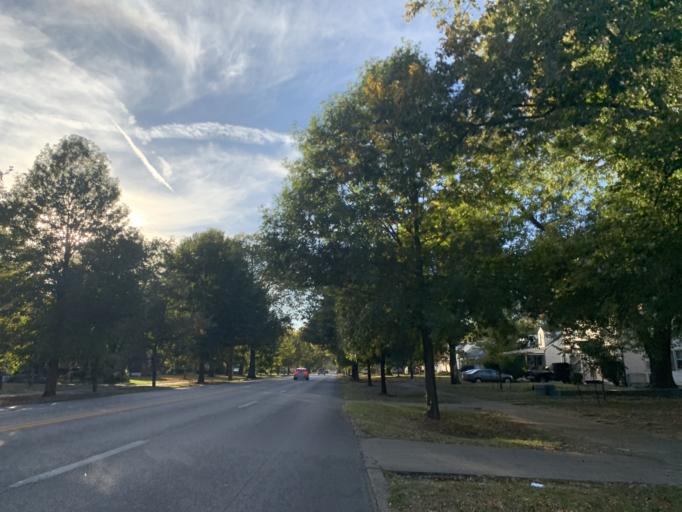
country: US
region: Kentucky
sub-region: Jefferson County
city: Shively
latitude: 38.2239
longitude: -85.8030
